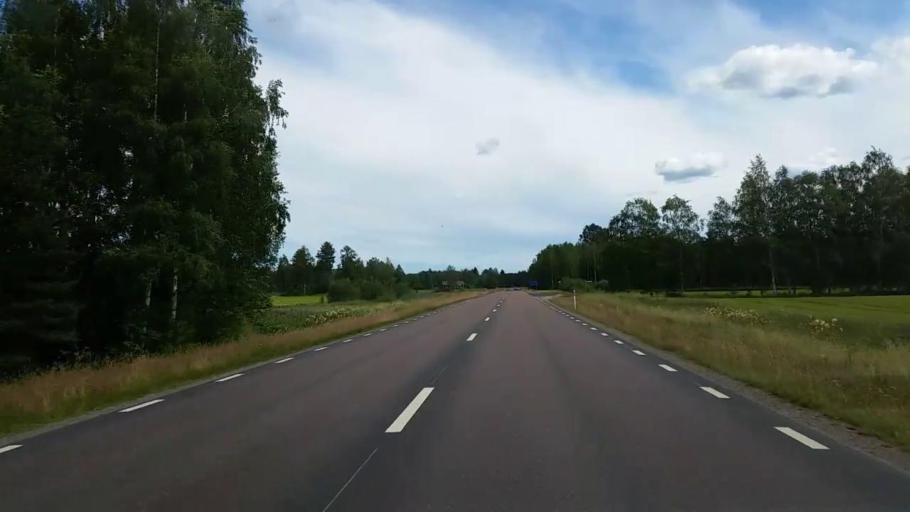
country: SE
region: Gaevleborg
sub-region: Ovanakers Kommun
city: Edsbyn
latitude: 61.3653
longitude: 15.8819
